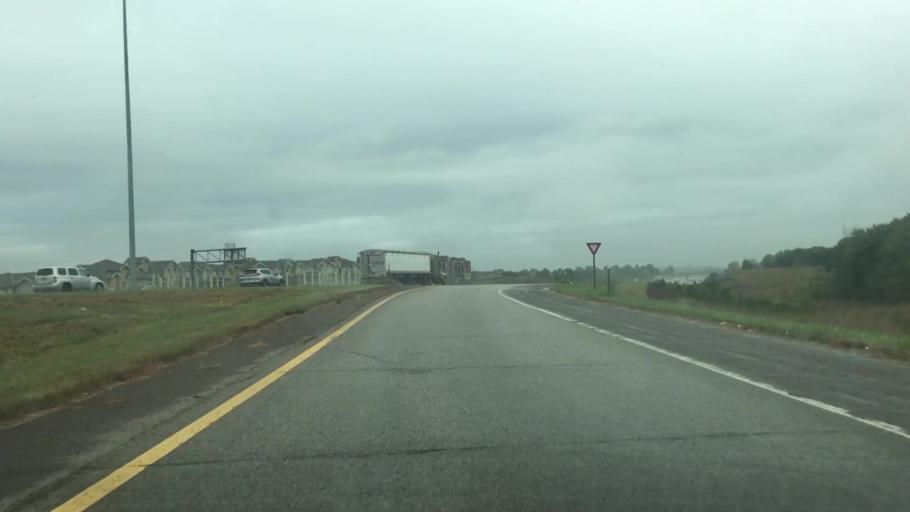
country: US
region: Kansas
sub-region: Johnson County
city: Lenexa
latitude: 38.9727
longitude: -94.7757
